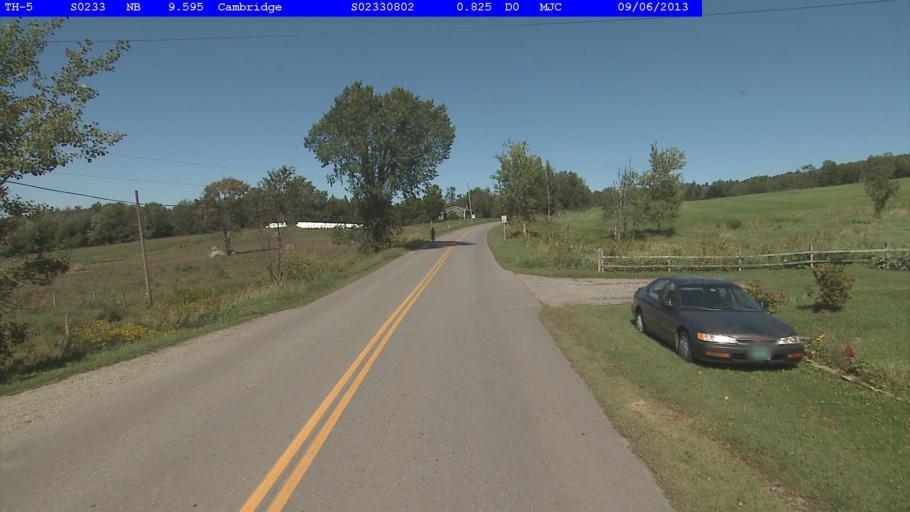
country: US
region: Vermont
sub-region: Chittenden County
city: Jericho
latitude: 44.5948
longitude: -72.8587
